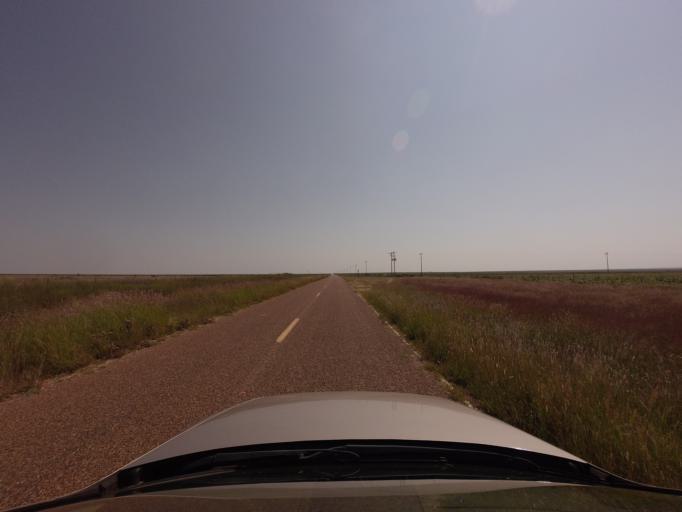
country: US
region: New Mexico
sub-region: Curry County
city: Cannon Air Force Base
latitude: 34.6329
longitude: -103.3917
